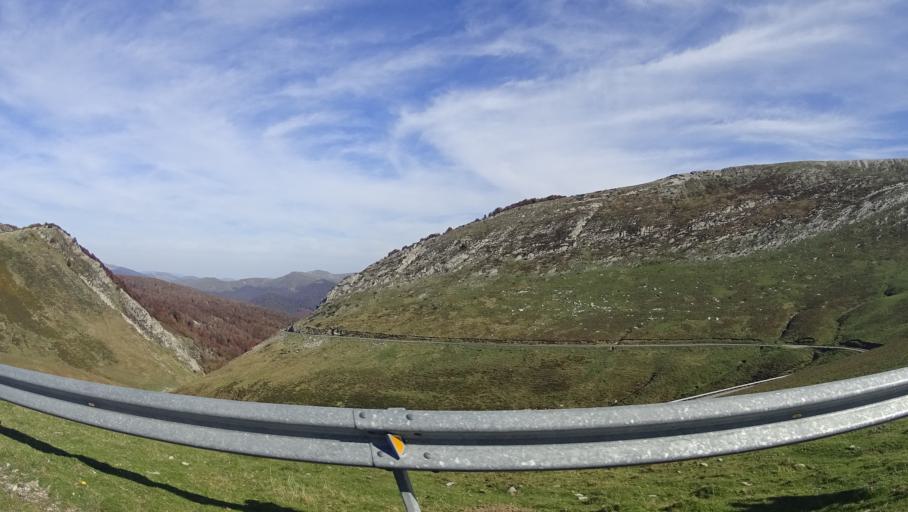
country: ES
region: Navarre
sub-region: Provincia de Navarra
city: Garaioa
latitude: 42.9570
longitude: -1.1392
